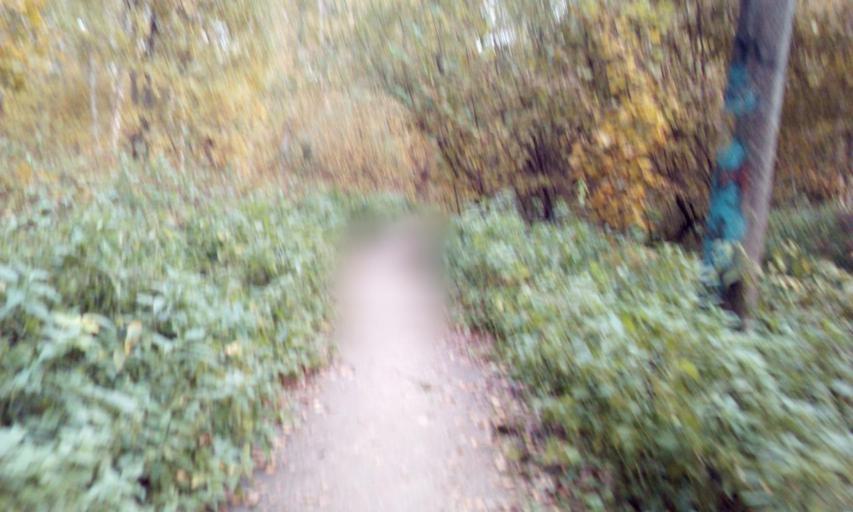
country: RU
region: Moskovskaya
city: Odintsovo
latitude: 55.6846
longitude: 37.2298
